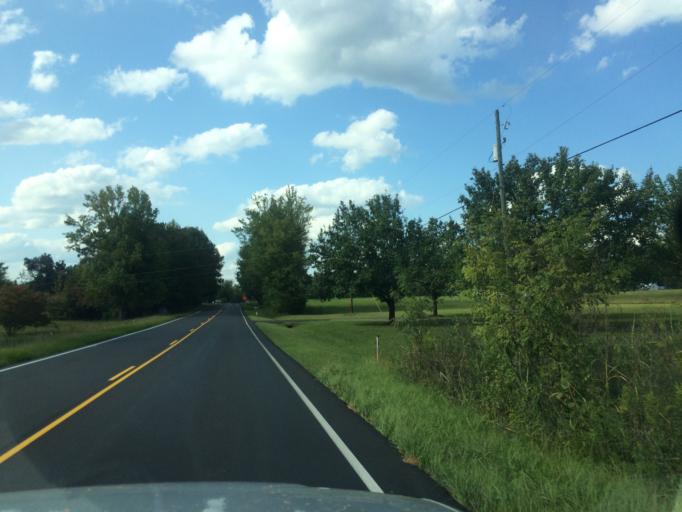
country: US
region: South Carolina
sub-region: Greenwood County
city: Ware Shoals
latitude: 34.4700
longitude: -82.1604
